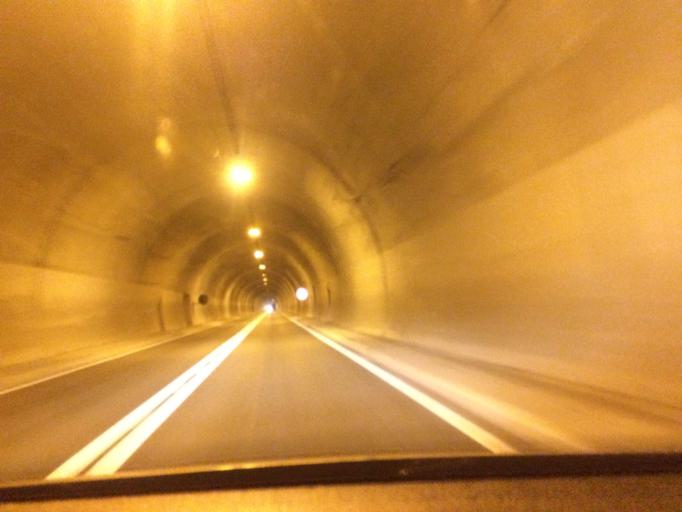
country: ME
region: Opstina Savnik
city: Savnik
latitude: 43.0438
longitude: 19.0795
